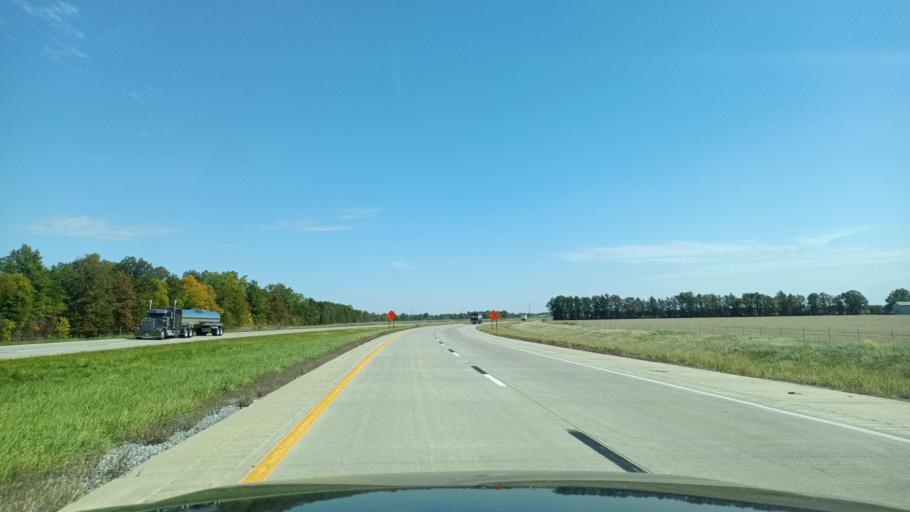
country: US
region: Ohio
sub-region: Paulding County
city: Paulding
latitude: 41.2103
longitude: -84.6268
